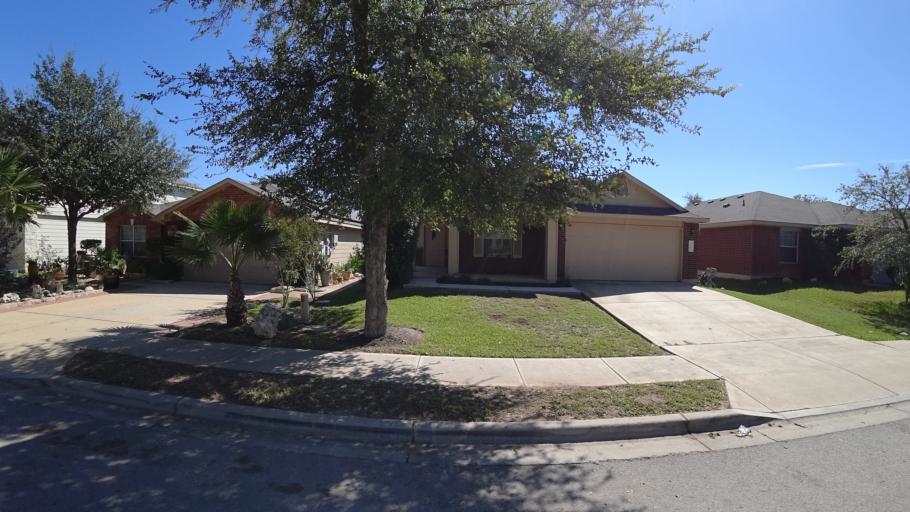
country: US
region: Texas
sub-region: Travis County
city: Hornsby Bend
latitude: 30.2737
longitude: -97.6311
